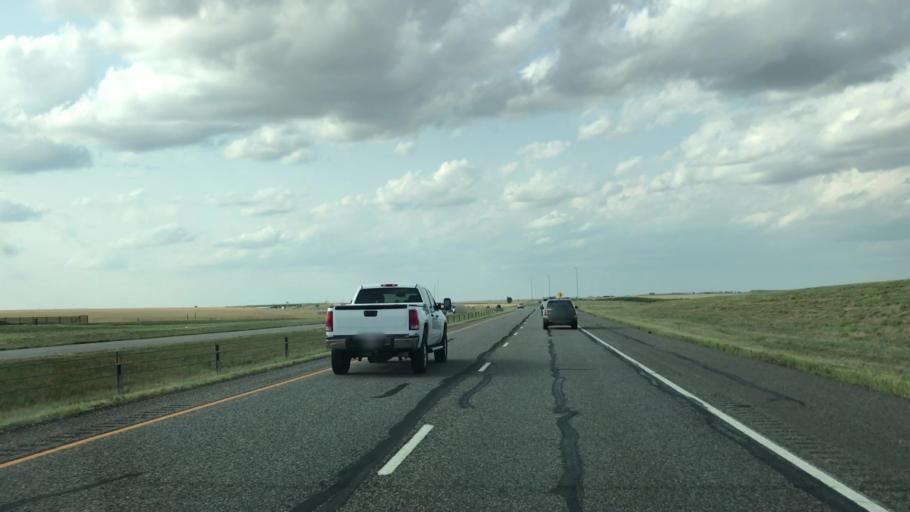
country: US
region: Colorado
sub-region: Adams County
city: Aurora
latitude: 39.8005
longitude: -104.7161
